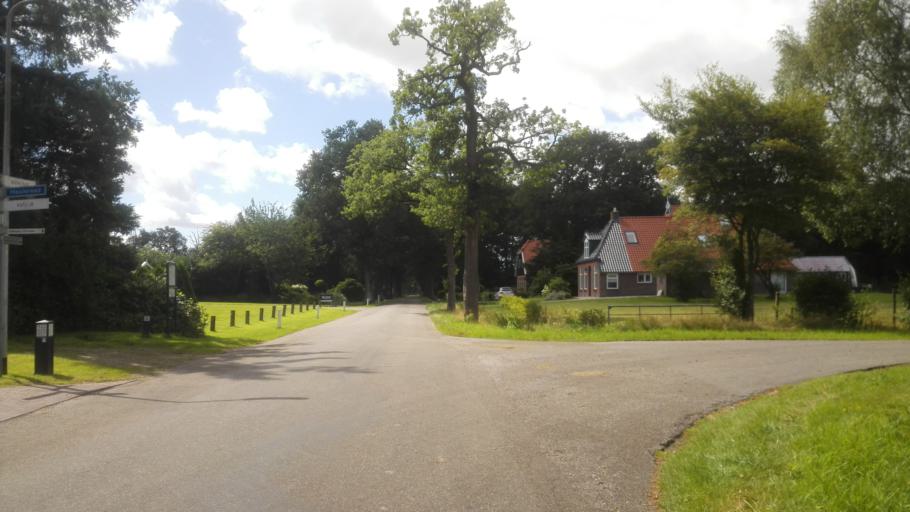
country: NL
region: Friesland
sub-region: Gemeente Weststellingwerf
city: Noordwolde
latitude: 52.9325
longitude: 6.1136
